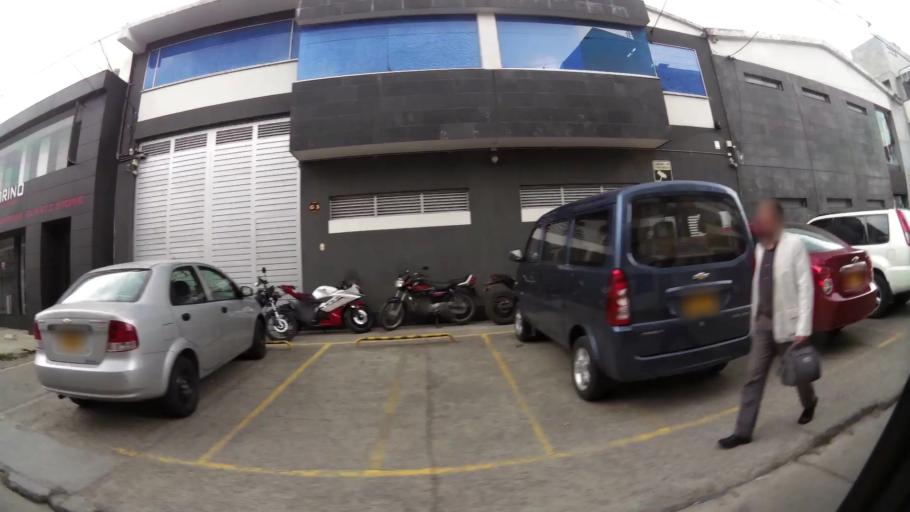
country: CO
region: Cundinamarca
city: La Calera
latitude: 4.7452
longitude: -74.0456
